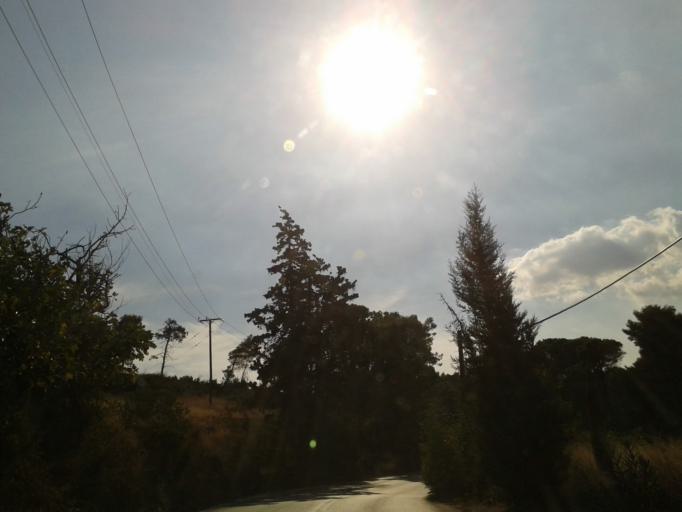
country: GR
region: Attica
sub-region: Nomarchia Anatolikis Attikis
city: Stamata
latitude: 38.1627
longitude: 23.9015
